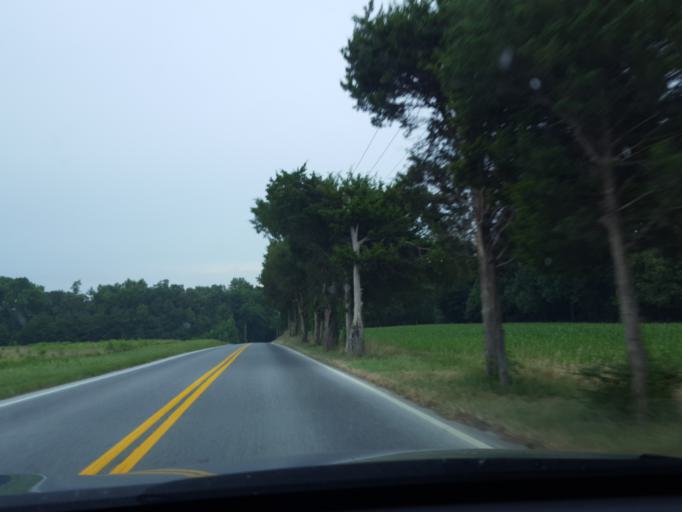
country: US
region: Maryland
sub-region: Saint Mary's County
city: Charlotte Hall
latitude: 38.4080
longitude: -76.8233
